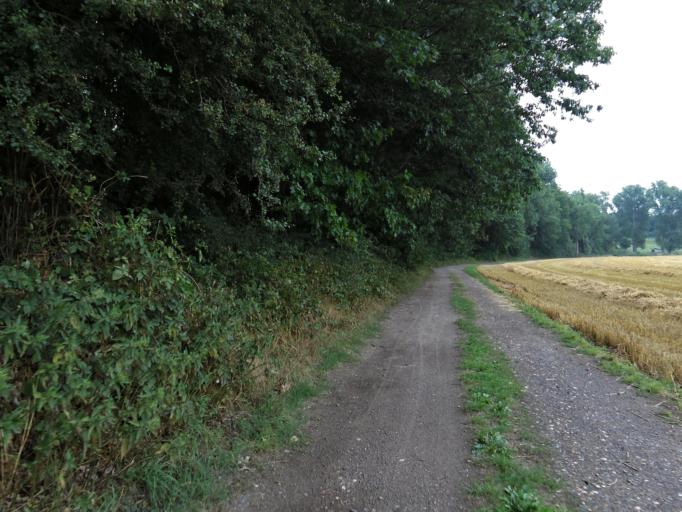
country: DE
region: North Rhine-Westphalia
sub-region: Regierungsbezirk Koln
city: Linnich
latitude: 50.9661
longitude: 6.2582
